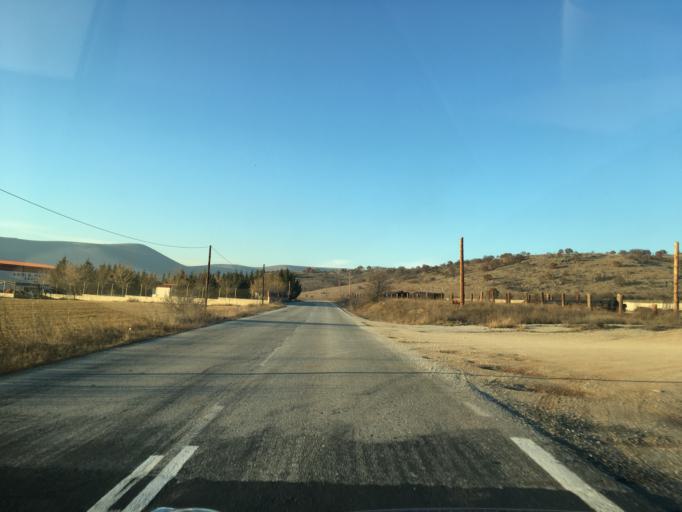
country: GR
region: West Macedonia
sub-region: Nomos Kozanis
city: Kozani
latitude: 40.3034
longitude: 21.7362
